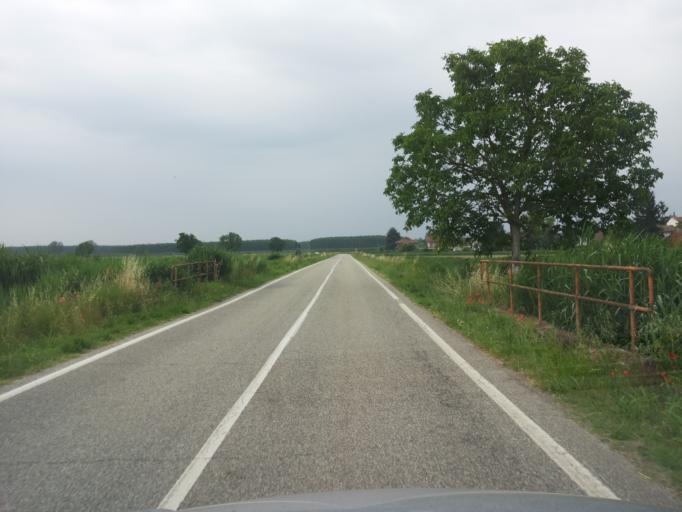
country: IT
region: Piedmont
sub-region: Provincia di Alessandria
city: Bozzole
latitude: 45.0696
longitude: 8.6031
